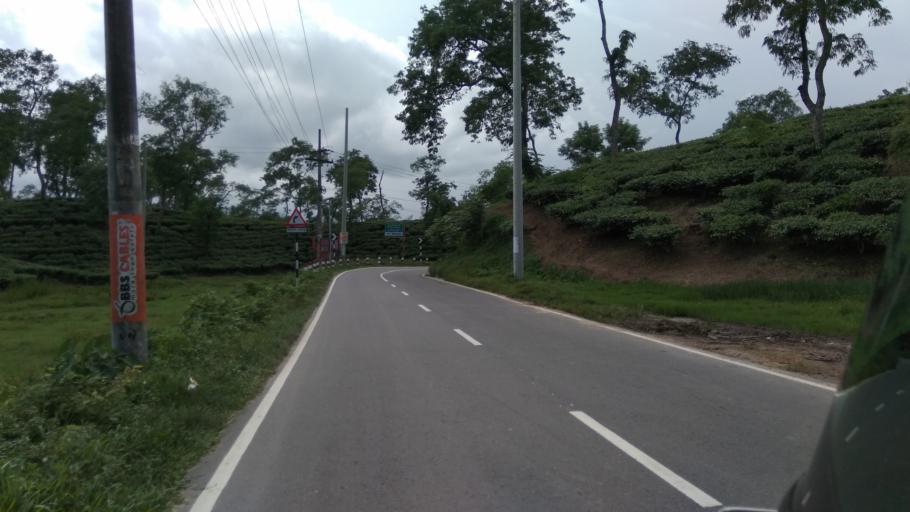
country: IN
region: Tripura
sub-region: Dhalai
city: Kamalpur
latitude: 24.2994
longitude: 91.7618
